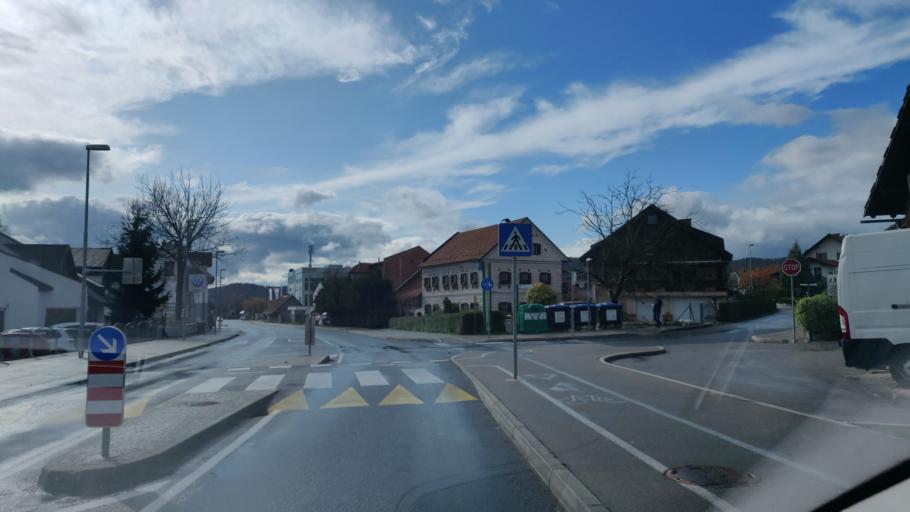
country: SI
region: Trzin
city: Trzin
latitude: 46.1313
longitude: 14.5608
